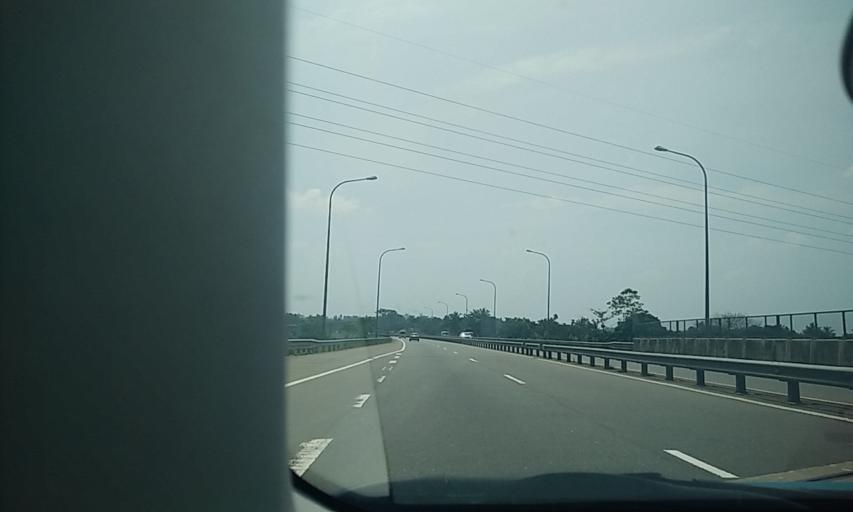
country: LK
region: Western
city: Homagama
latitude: 6.7777
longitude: 79.9803
